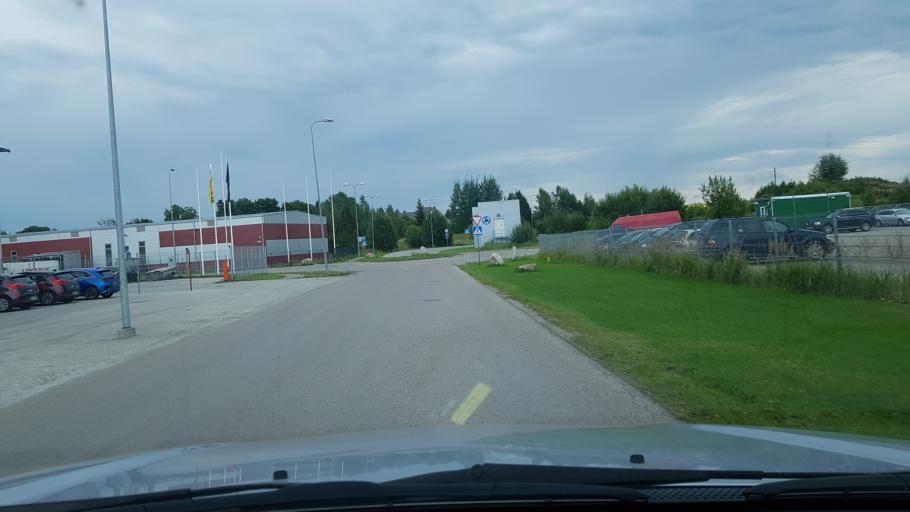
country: EE
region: Harju
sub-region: Rae vald
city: Jueri
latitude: 59.3481
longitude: 24.8955
